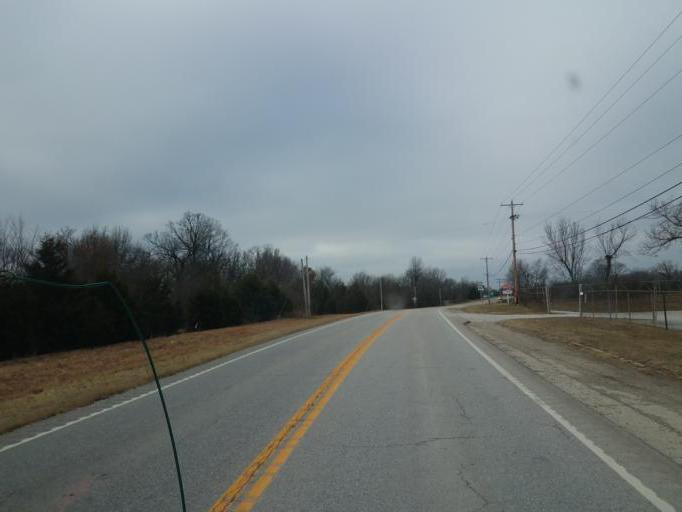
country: US
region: Missouri
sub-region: Greene County
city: Strafford
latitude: 37.2476
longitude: -93.1779
